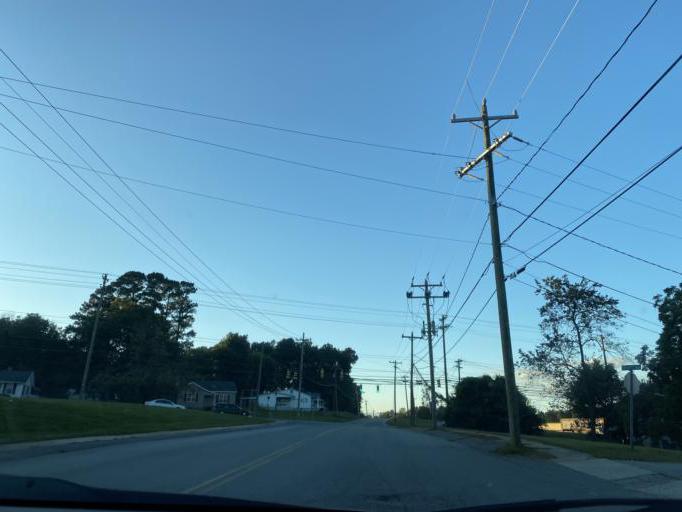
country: US
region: South Carolina
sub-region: Cherokee County
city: East Gaffney
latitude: 35.0830
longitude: -81.6395
